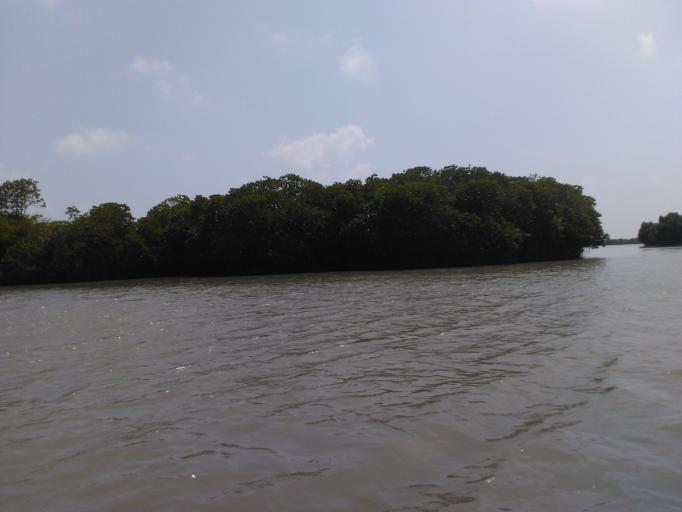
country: IN
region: Tamil Nadu
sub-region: Cuddalore
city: Annamalainagar
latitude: 11.4398
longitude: 79.7864
